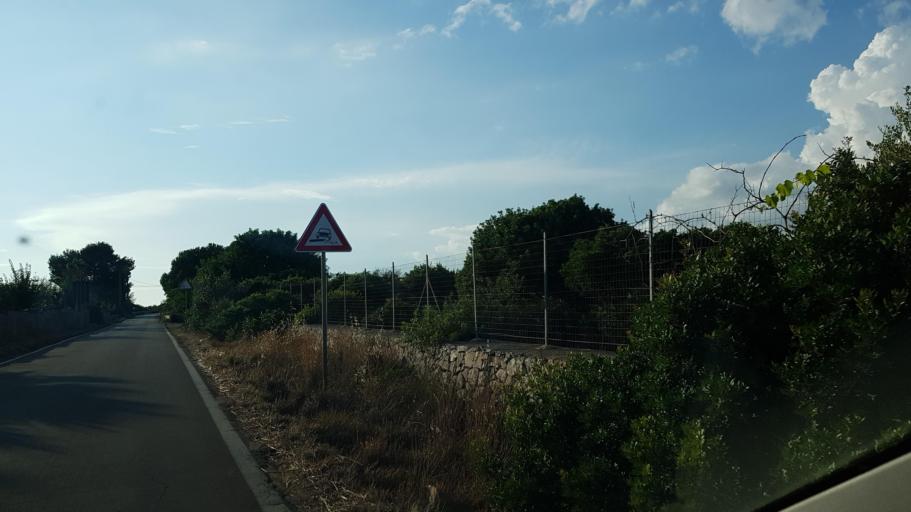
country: IT
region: Apulia
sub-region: Provincia di Lecce
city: Gemini
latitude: 39.8457
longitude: 18.2093
